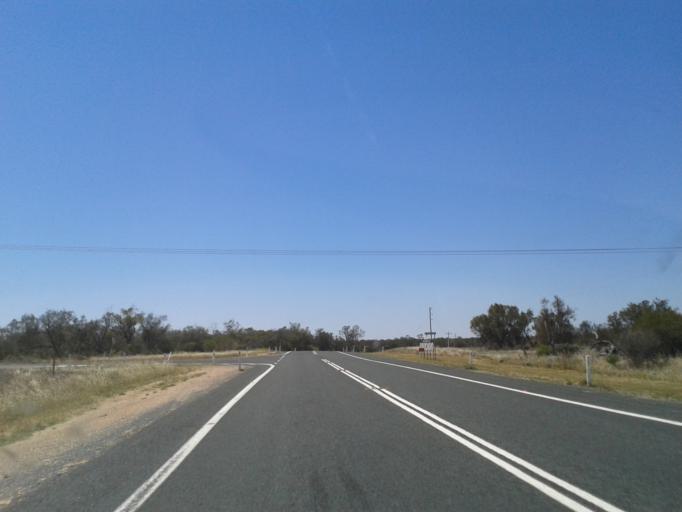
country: AU
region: New South Wales
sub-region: Wentworth
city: Dareton
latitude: -34.0983
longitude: 142.0890
